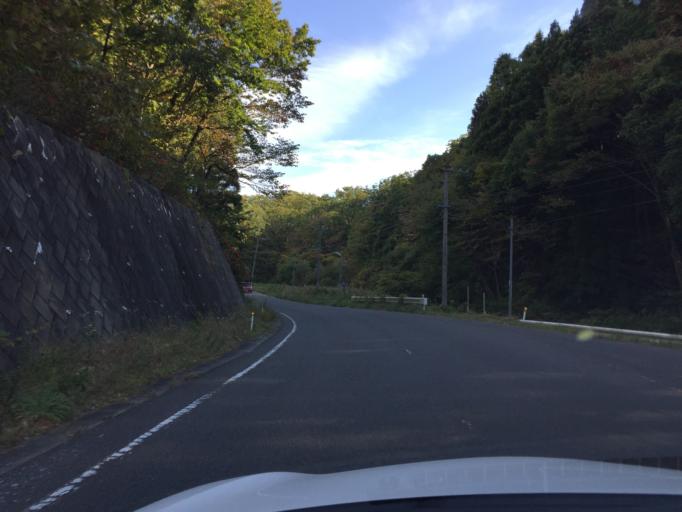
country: JP
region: Fukushima
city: Miharu
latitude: 37.3592
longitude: 140.5325
